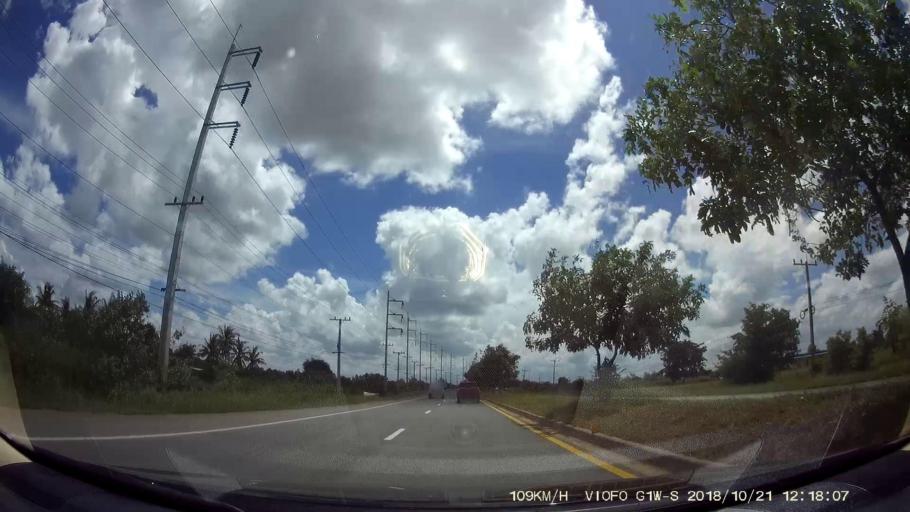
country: TH
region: Nakhon Ratchasima
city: Dan Khun Thot
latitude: 15.3217
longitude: 101.8180
